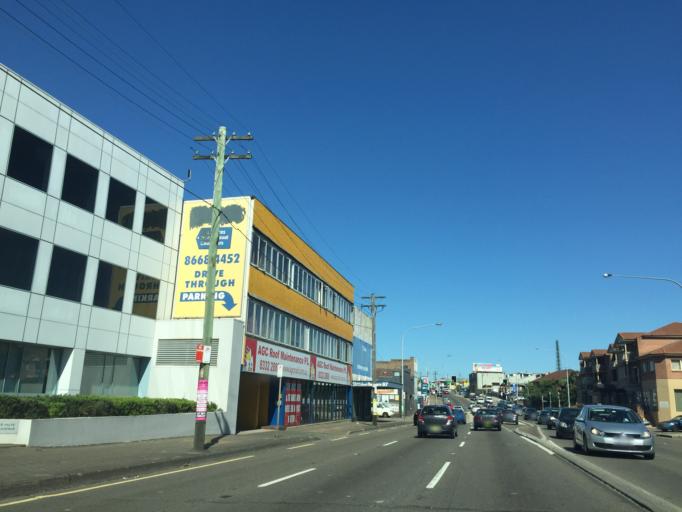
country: AU
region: New South Wales
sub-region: Strathfield
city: Homebush
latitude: -33.8677
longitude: 151.0978
